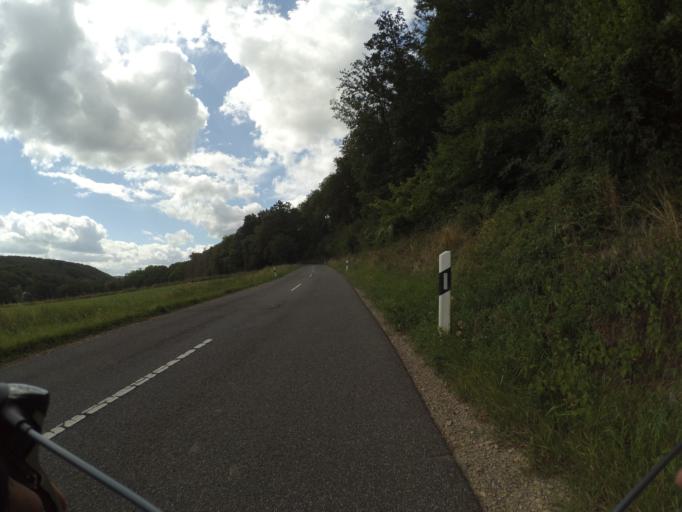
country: DE
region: North Rhine-Westphalia
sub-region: Regierungsbezirk Koln
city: Langerwehe
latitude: 50.7883
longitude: 6.3320
